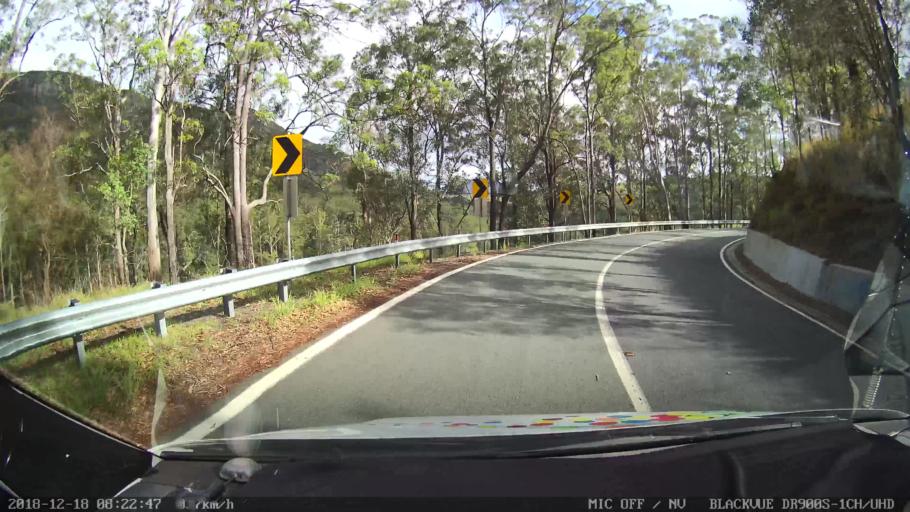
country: AU
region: New South Wales
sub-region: Kyogle
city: Kyogle
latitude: -28.3235
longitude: 152.7255
